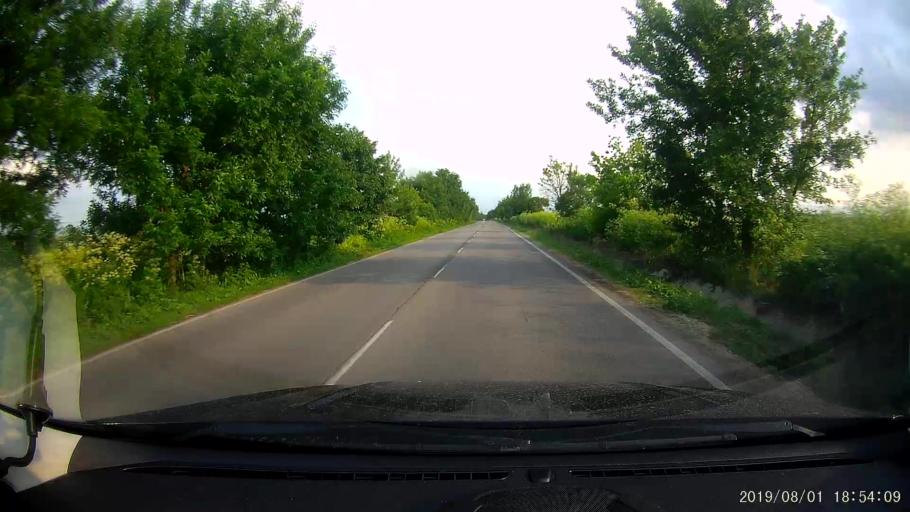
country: BG
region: Shumen
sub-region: Obshtina Shumen
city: Shumen
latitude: 43.2057
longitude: 26.9999
